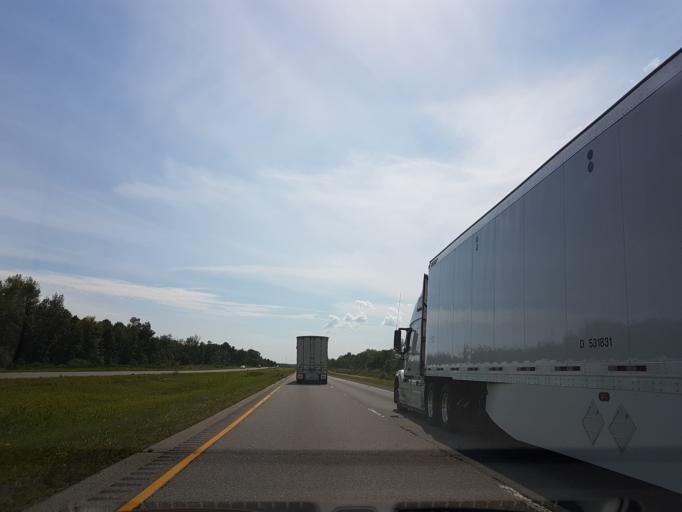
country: CA
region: Ontario
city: Prescott
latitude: 44.6801
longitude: -75.5938
